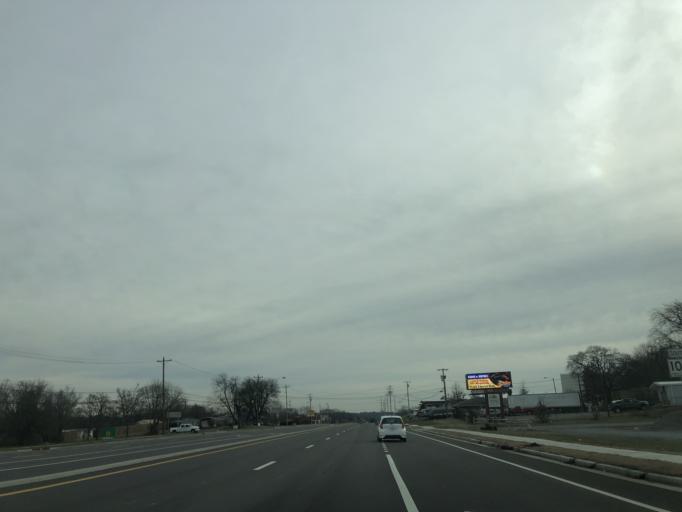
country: US
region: Tennessee
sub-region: Sumner County
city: Gallatin
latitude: 36.3627
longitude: -86.4400
